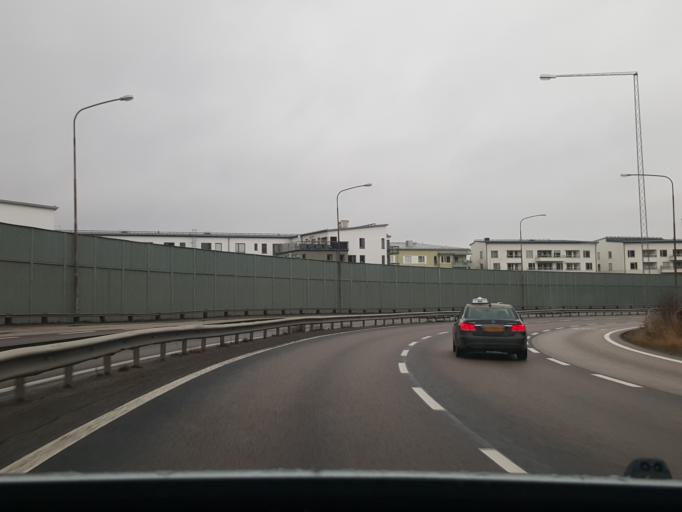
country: SE
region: Stockholm
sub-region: Stockholms Kommun
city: OEstermalm
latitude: 59.3090
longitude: 18.1062
